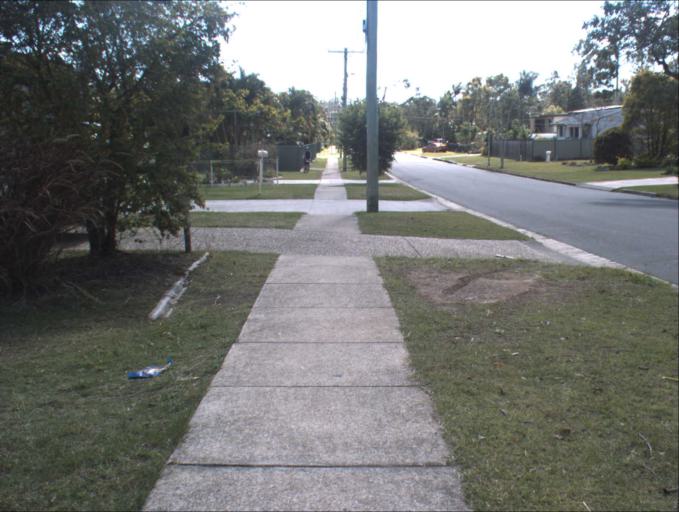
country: AU
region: Queensland
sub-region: Logan
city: Waterford West
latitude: -27.6715
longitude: 153.1071
